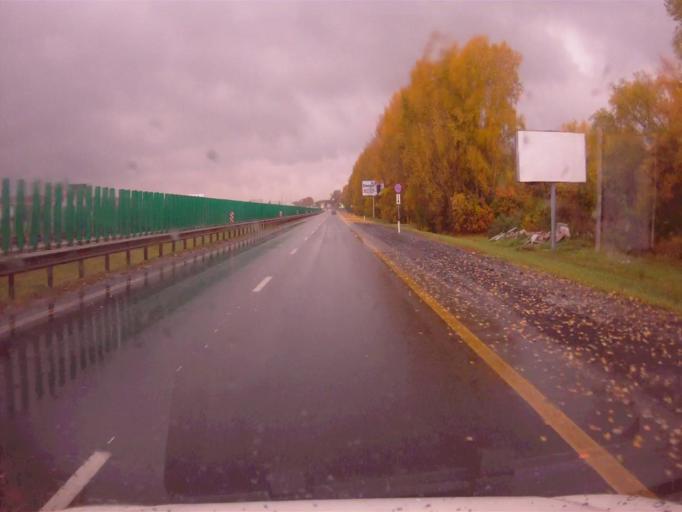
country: RU
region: Chelyabinsk
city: Dolgoderevenskoye
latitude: 55.2789
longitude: 61.3435
